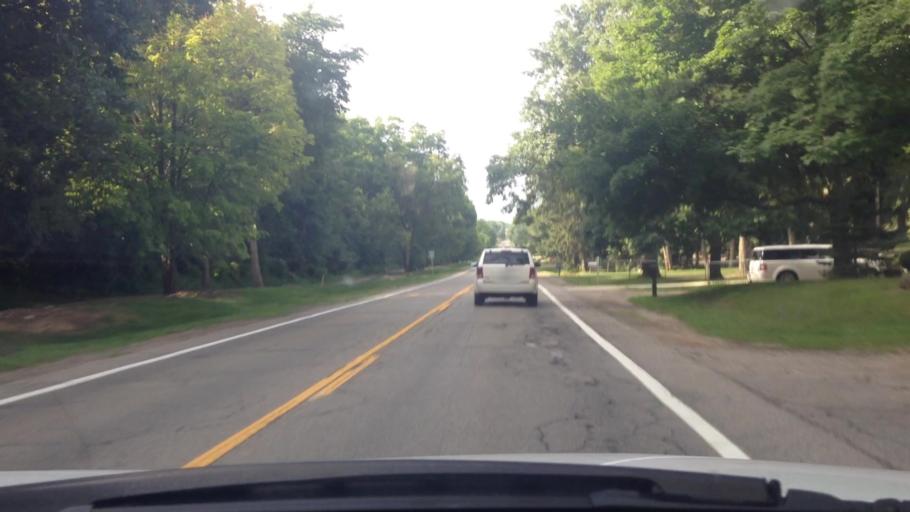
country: US
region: Michigan
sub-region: Oakland County
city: Clarkston
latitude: 42.7416
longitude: -83.3503
